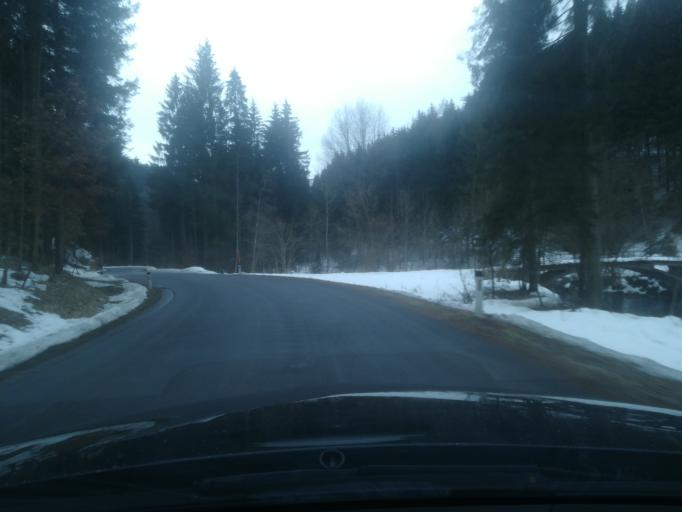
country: AT
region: Upper Austria
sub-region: Politischer Bezirk Perg
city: Perg
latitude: 48.4092
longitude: 14.6344
